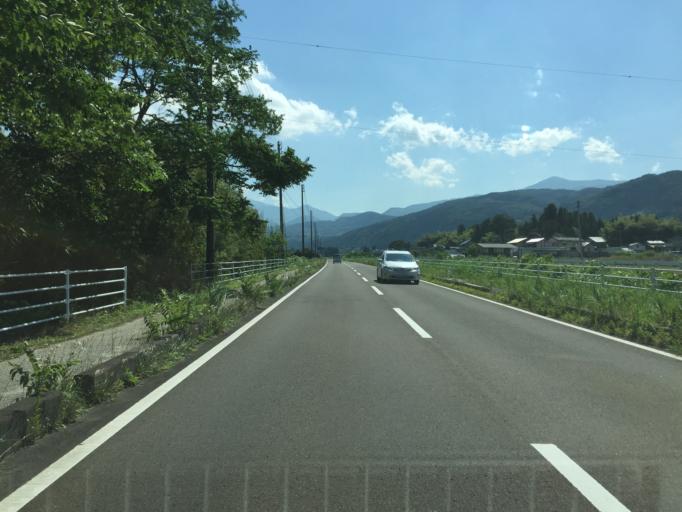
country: JP
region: Fukushima
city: Fukushima-shi
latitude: 37.7364
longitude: 140.3732
